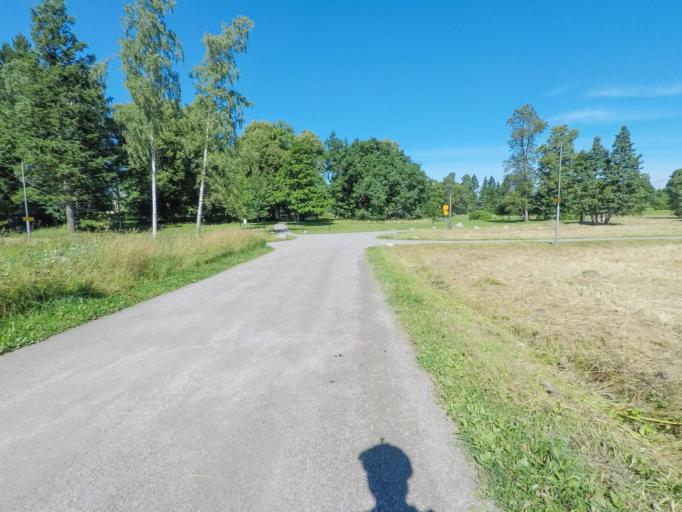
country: FI
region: Uusimaa
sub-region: Helsinki
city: Helsinki
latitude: 60.1780
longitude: 25.0332
